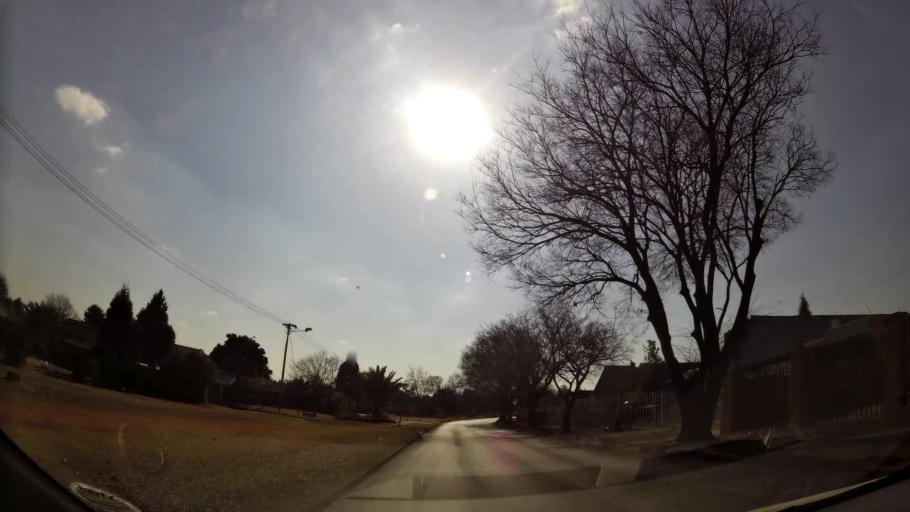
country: ZA
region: Gauteng
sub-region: West Rand District Municipality
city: Randfontein
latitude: -26.1581
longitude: 27.6924
